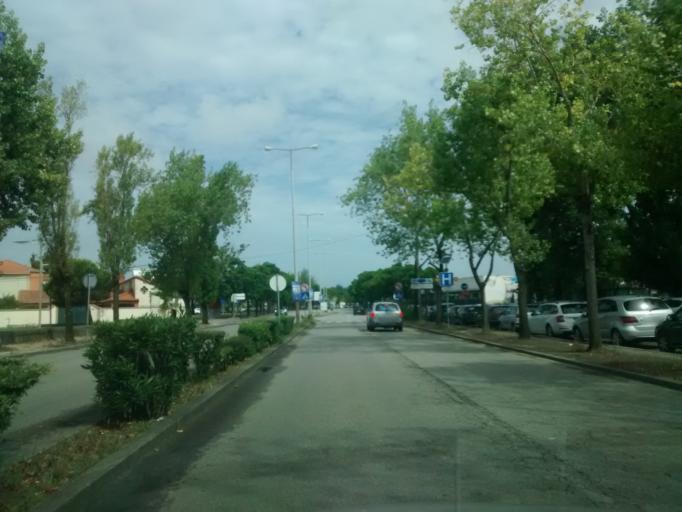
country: PT
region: Aveiro
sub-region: Aveiro
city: Aveiro
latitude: 40.6326
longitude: -8.6554
